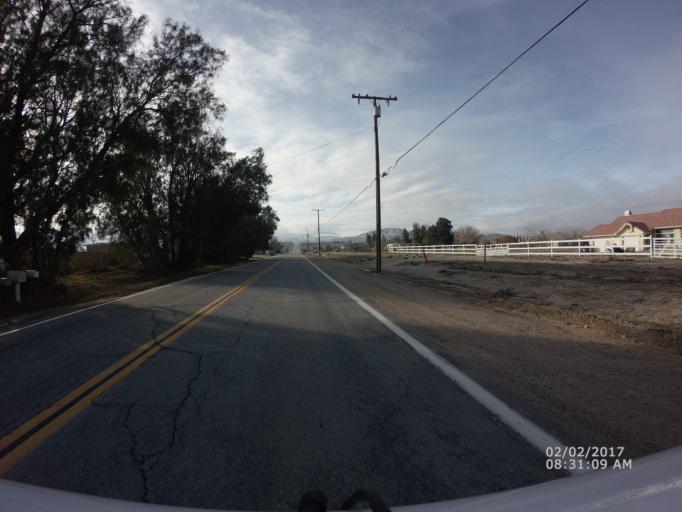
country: US
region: California
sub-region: Los Angeles County
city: Littlerock
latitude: 34.5379
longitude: -118.0277
